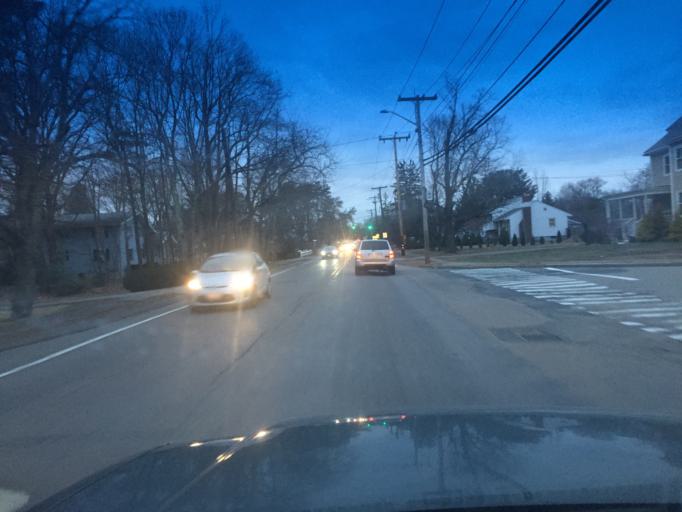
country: US
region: Massachusetts
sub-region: Norfolk County
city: Norwood
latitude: 42.1761
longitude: -71.1776
